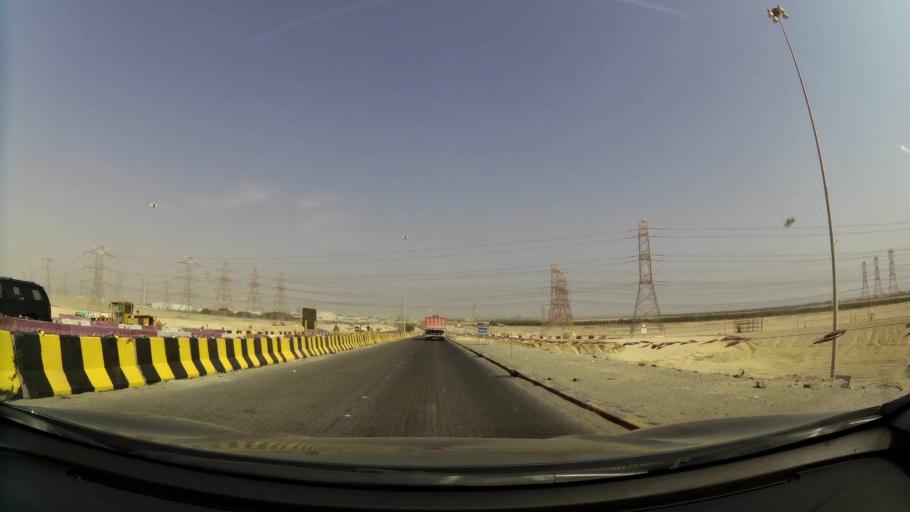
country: KW
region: Al Ahmadi
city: Al Fahahil
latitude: 28.9609
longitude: 48.1231
